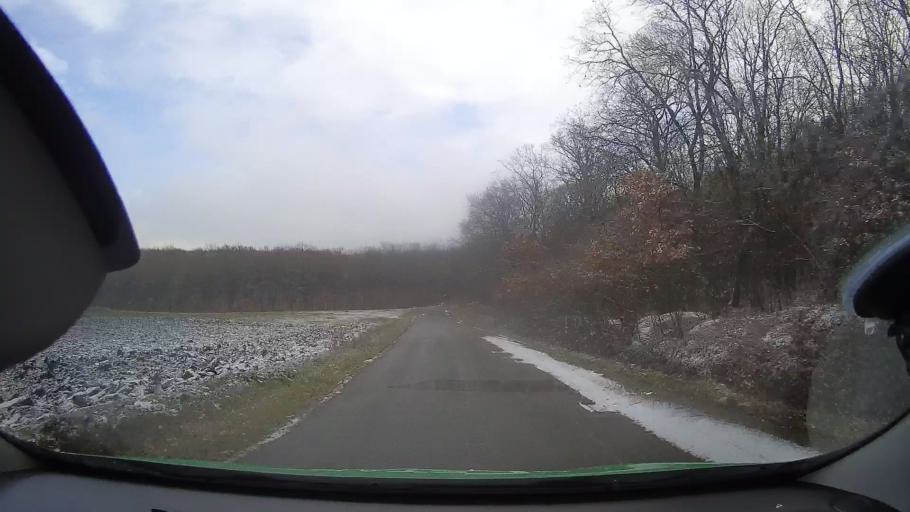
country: RO
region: Mures
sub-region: Comuna Ludus
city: Gheja
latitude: 46.4014
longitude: 24.0161
